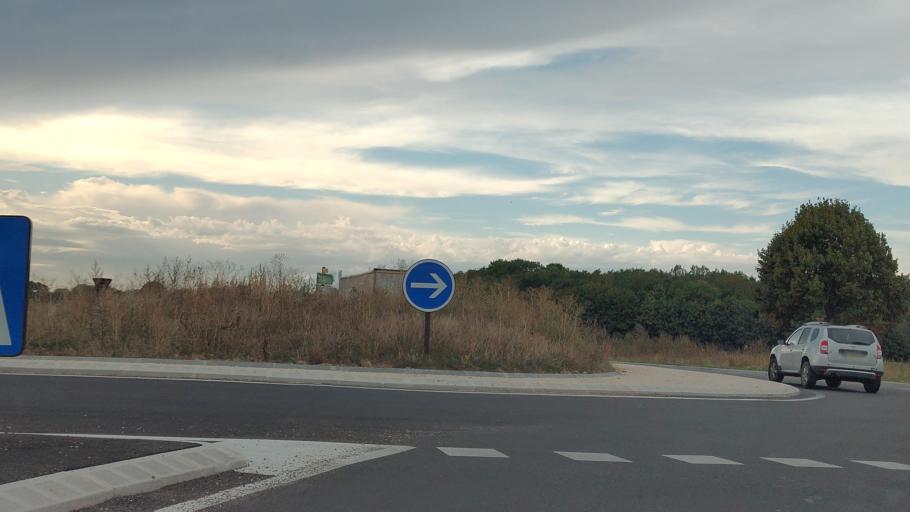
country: FR
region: Ile-de-France
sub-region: Departement de Seine-et-Marne
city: Guignes
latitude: 48.6269
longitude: 2.8192
